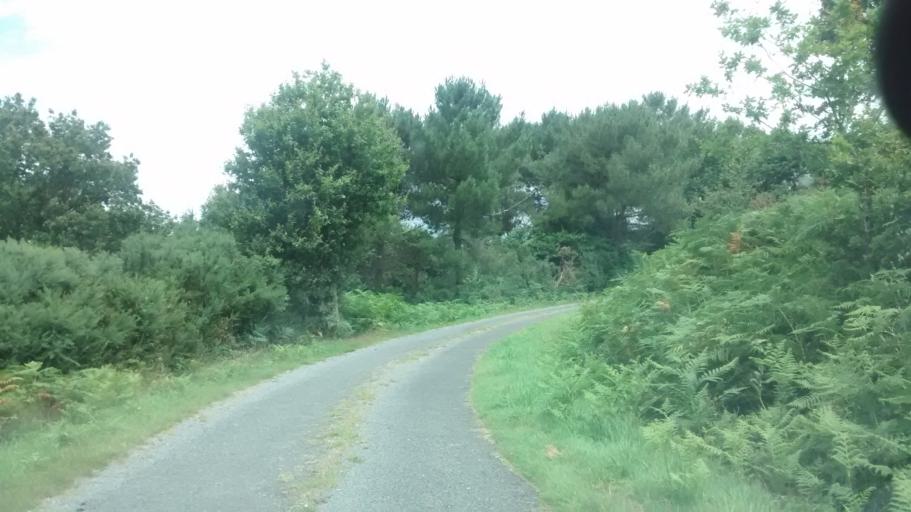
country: FR
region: Brittany
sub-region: Departement d'Ille-et-Vilaine
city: La Dominelais
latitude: 47.7889
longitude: -1.7199
